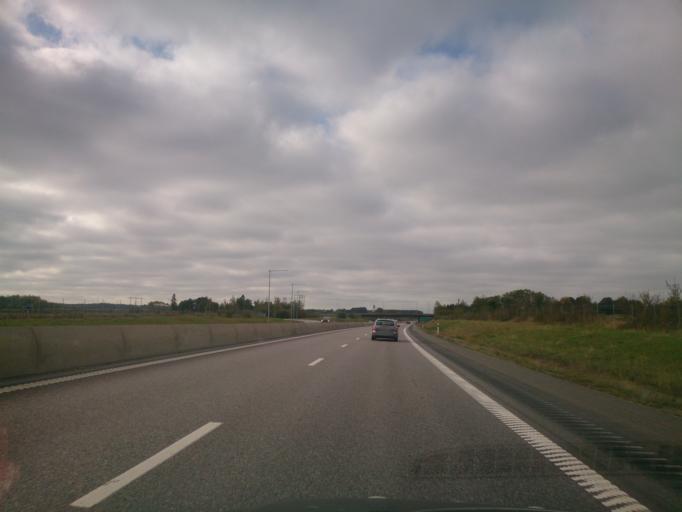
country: SE
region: OEstergoetland
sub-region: Norrkopings Kommun
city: Norrkoping
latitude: 58.5828
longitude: 16.1193
